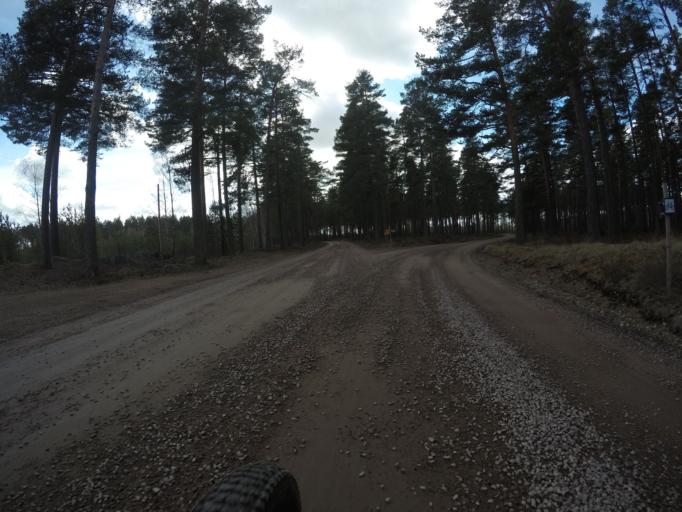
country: SE
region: Vaestmanland
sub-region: Kungsors Kommun
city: Kungsoer
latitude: 59.3738
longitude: 16.1028
